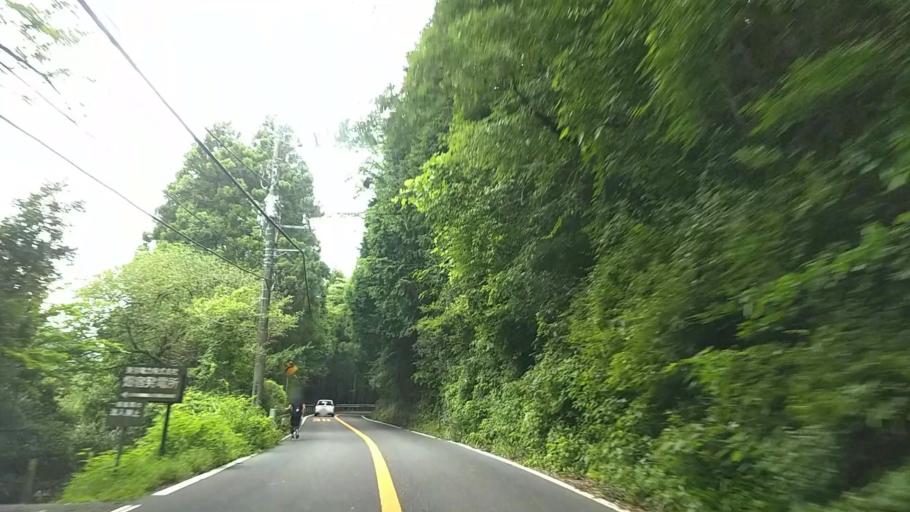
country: JP
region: Kanagawa
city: Hakone
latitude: 35.2180
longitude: 139.0699
